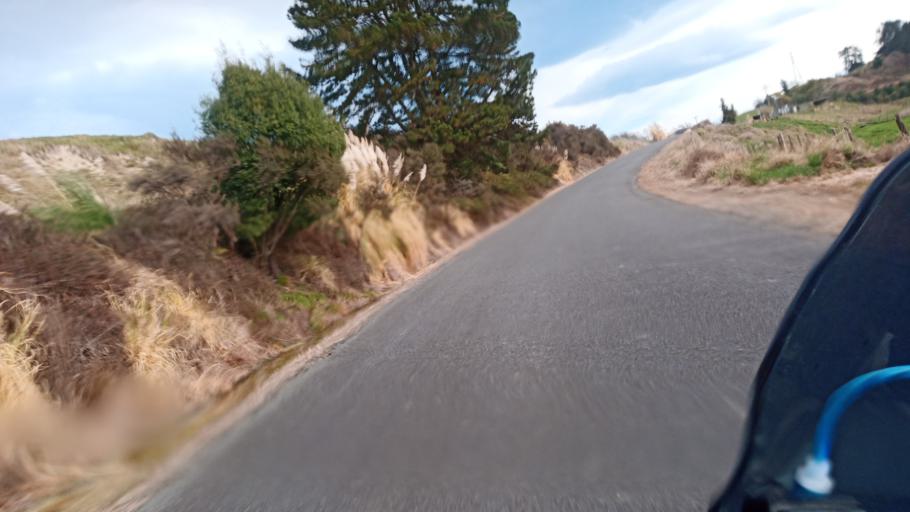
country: NZ
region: Hawke's Bay
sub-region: Wairoa District
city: Wairoa
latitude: -38.9728
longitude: 177.4355
